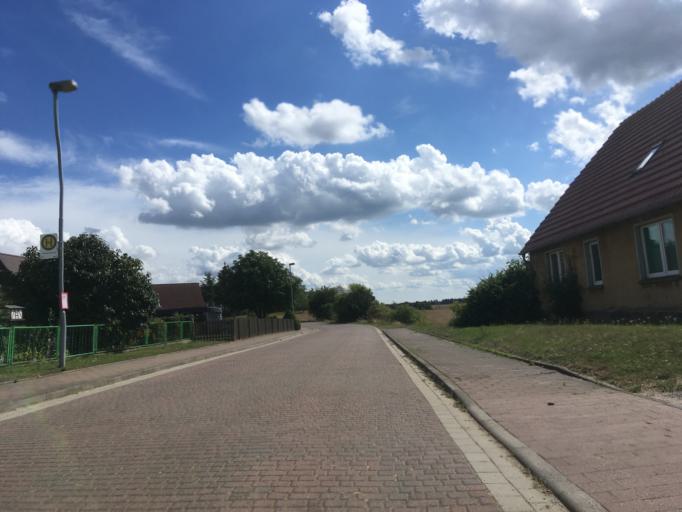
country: DE
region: Brandenburg
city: Gerswalde
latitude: 53.0940
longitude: 13.8717
